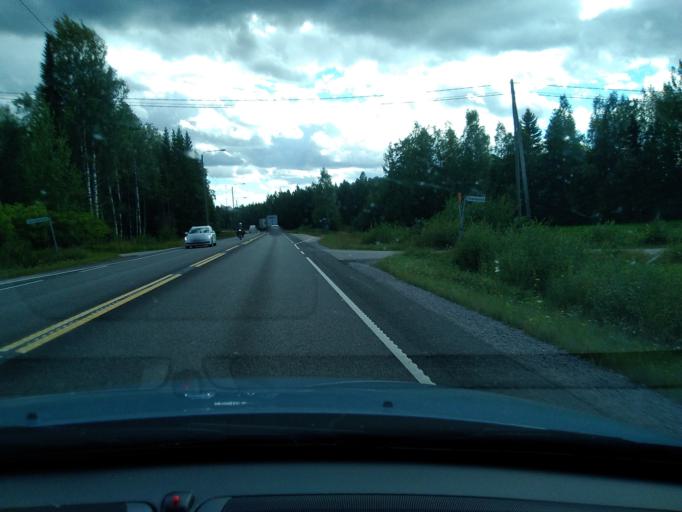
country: FI
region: Central Finland
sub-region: AEaenekoski
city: AEaenekoski
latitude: 62.4582
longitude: 25.6716
